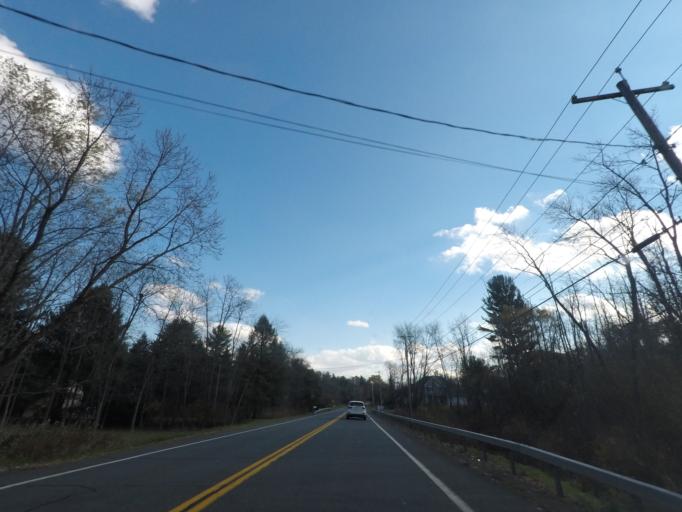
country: US
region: New York
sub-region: Schenectady County
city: Niskayuna
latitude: 42.8016
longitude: -73.8594
